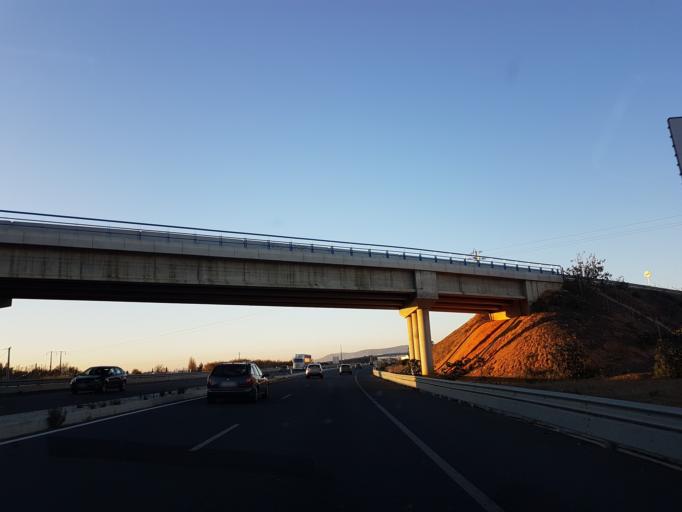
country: PT
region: Faro
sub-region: Faro
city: Faro
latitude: 37.0349
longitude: -7.9189
